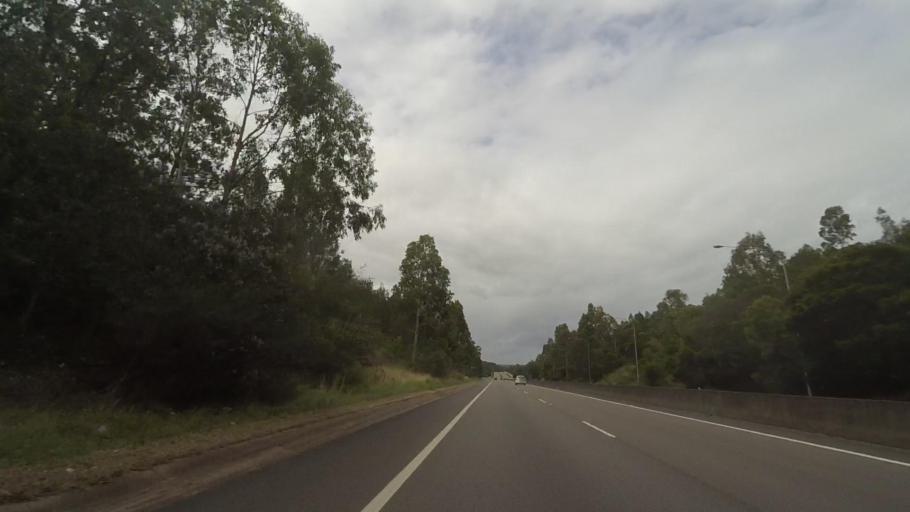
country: AU
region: New South Wales
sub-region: Port Stephens Shire
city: Raymond Terrace
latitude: -32.7618
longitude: 151.7640
